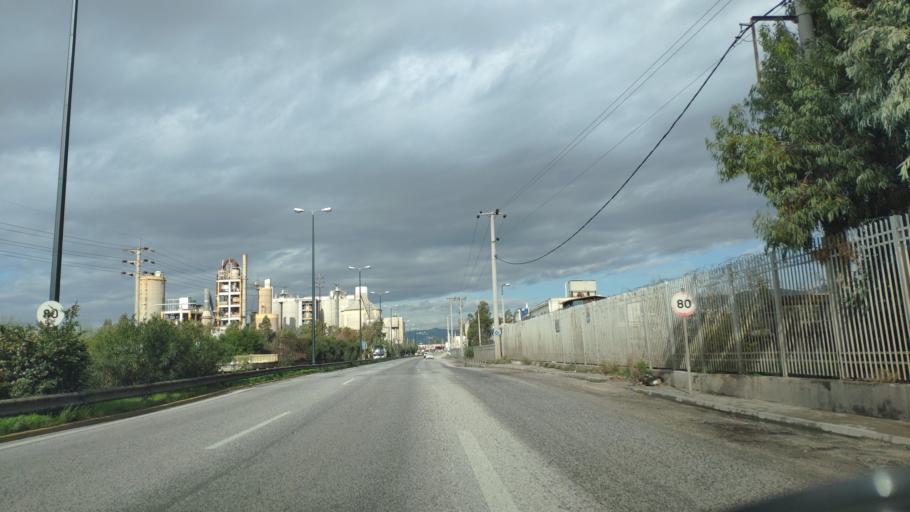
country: GR
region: Attica
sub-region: Nomarchia Athinas
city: Skaramangas
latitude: 38.0314
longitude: 23.5964
